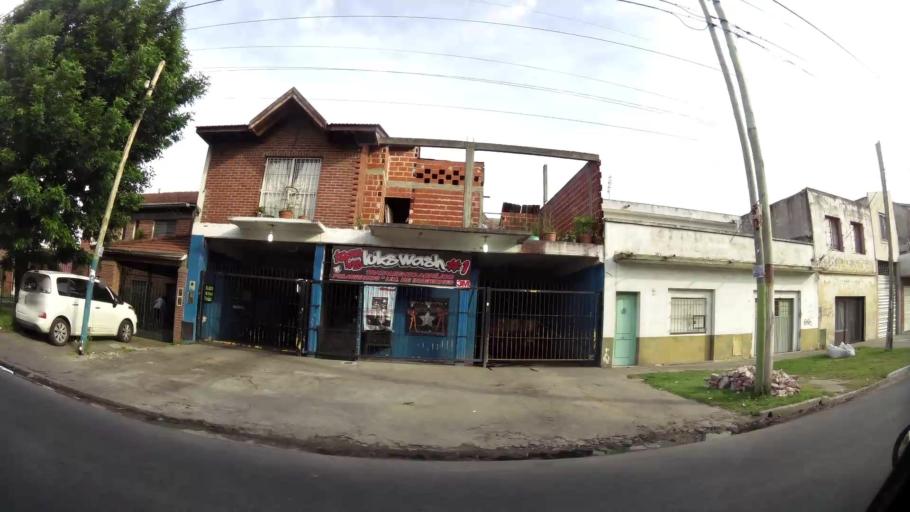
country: AR
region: Buenos Aires
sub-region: Partido de Quilmes
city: Quilmes
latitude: -34.7398
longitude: -58.2659
